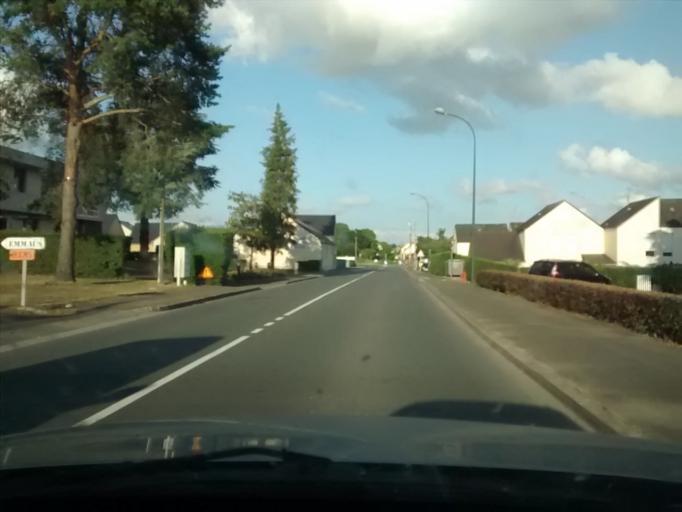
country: FR
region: Pays de la Loire
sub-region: Departement de la Mayenne
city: Evron
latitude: 48.1573
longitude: -0.4148
